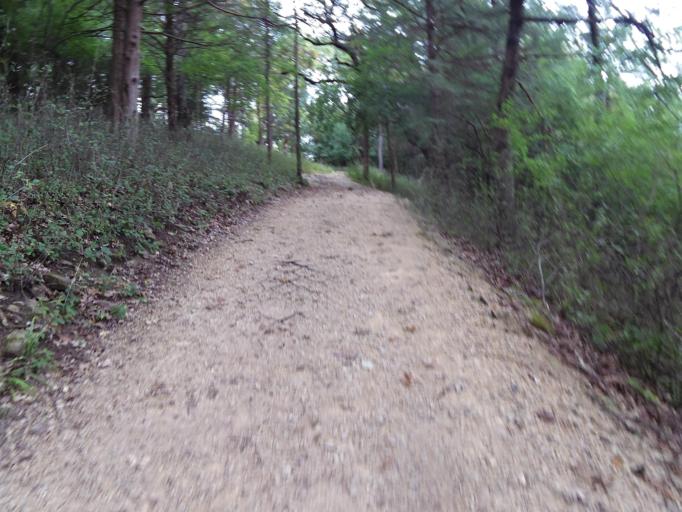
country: US
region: Minnesota
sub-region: Washington County
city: Afton
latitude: 44.8633
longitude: -92.7779
